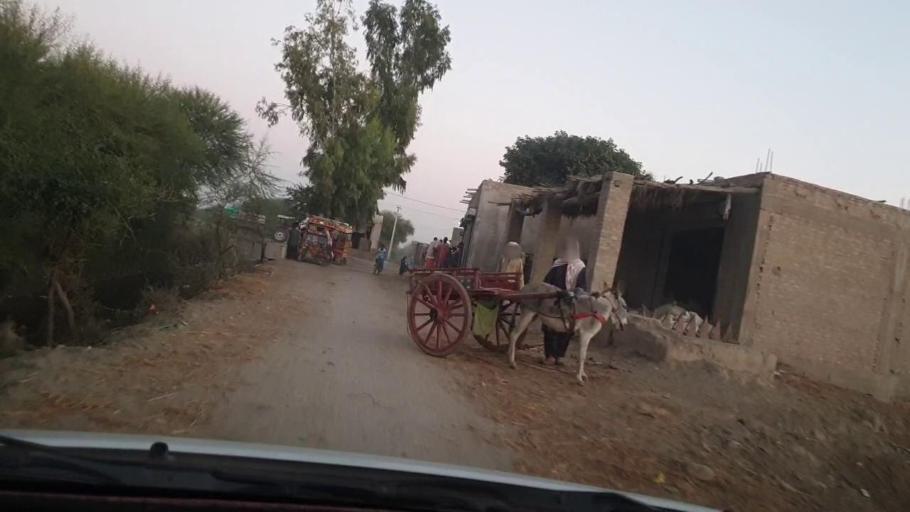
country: PK
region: Sindh
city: Khairpur Nathan Shah
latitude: 27.1454
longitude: 67.7059
